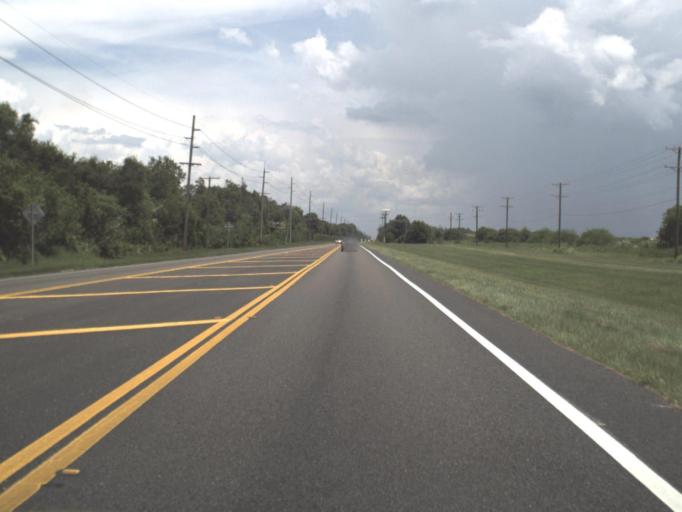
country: US
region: Florida
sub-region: Hillsborough County
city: Sun City Center
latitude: 27.7184
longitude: -82.3352
